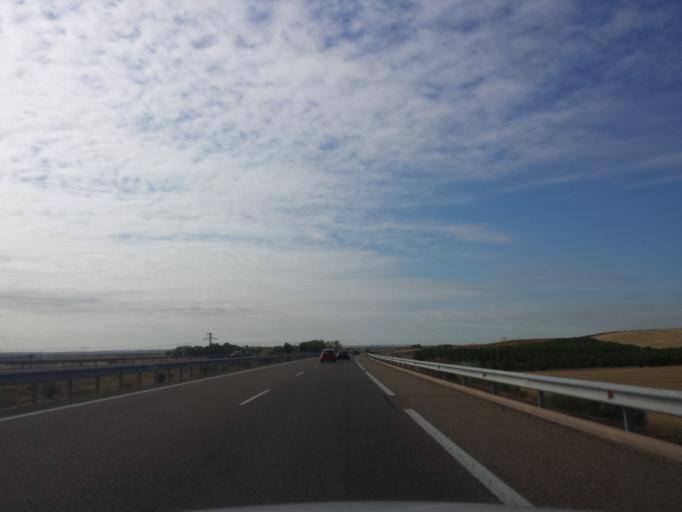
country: ES
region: Castille and Leon
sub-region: Provincia de Leon
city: Ardon
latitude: 42.4649
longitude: -5.5838
